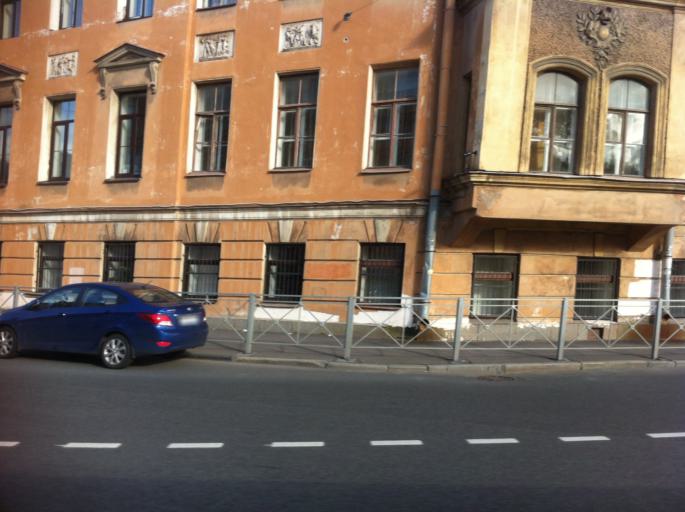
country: RU
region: St.-Petersburg
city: Admiralteisky
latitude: 59.9180
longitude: 30.2804
